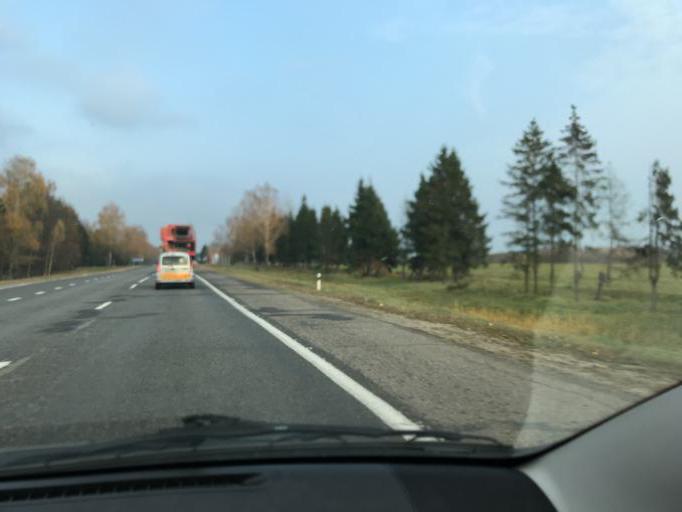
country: BY
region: Vitebsk
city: Syanno
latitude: 55.1404
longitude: 29.8238
